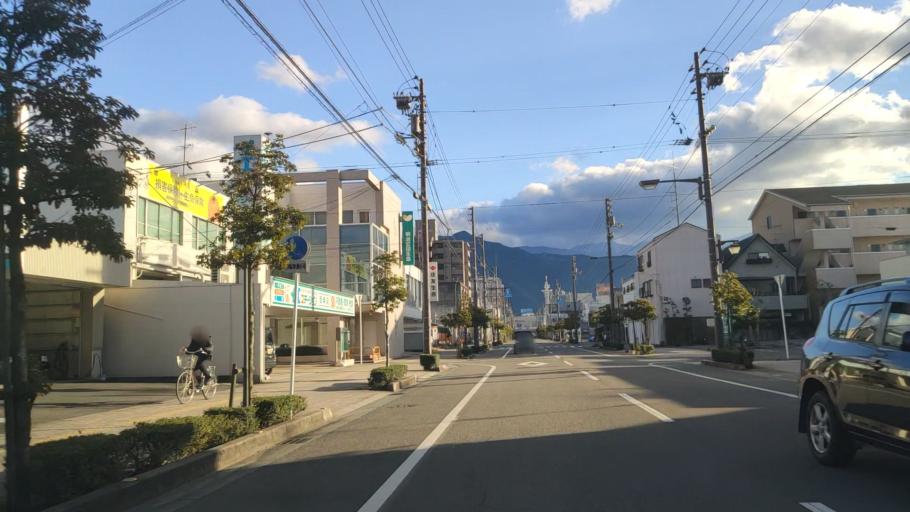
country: JP
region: Ehime
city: Saijo
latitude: 33.9163
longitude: 133.1862
